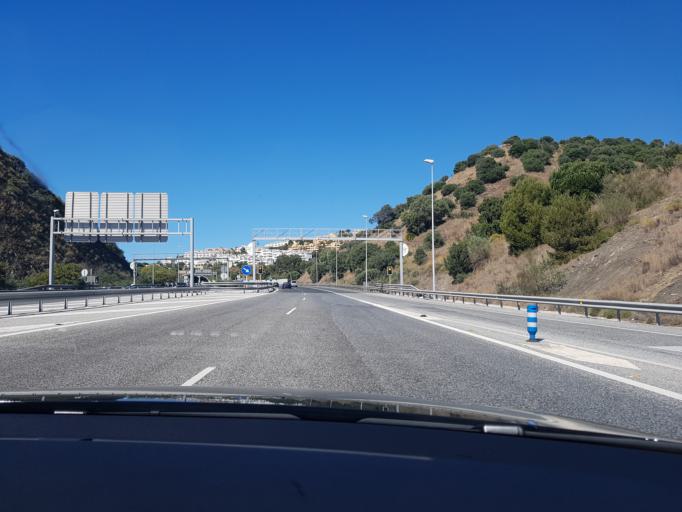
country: ES
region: Andalusia
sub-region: Provincia de Malaga
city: Fuengirola
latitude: 36.5064
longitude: -4.7196
